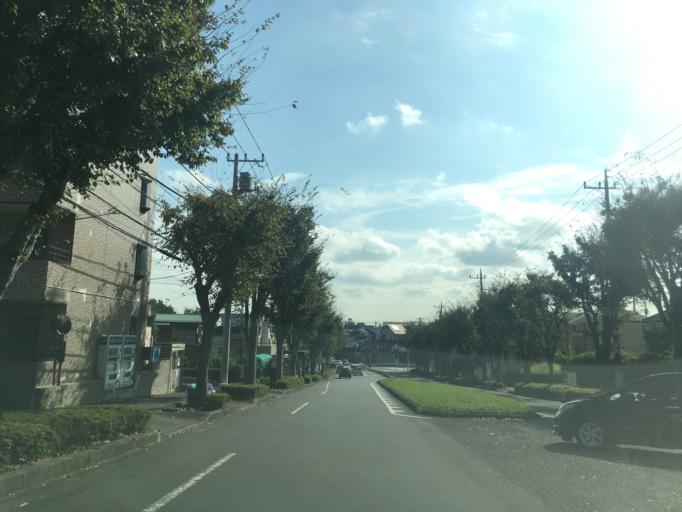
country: JP
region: Tokyo
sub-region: Machida-shi
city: Machida
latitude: 35.5803
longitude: 139.4114
